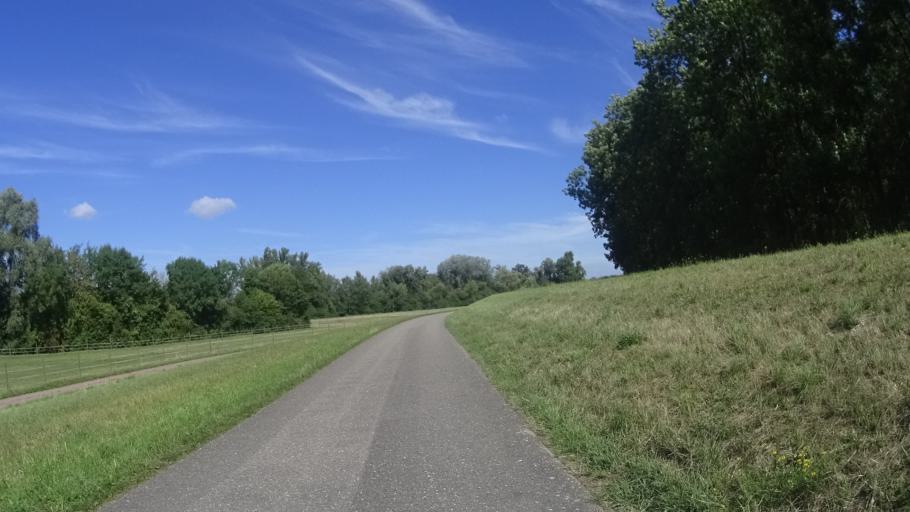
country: DE
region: Rheinland-Pfalz
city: Leimersheim
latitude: 49.1294
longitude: 8.3555
